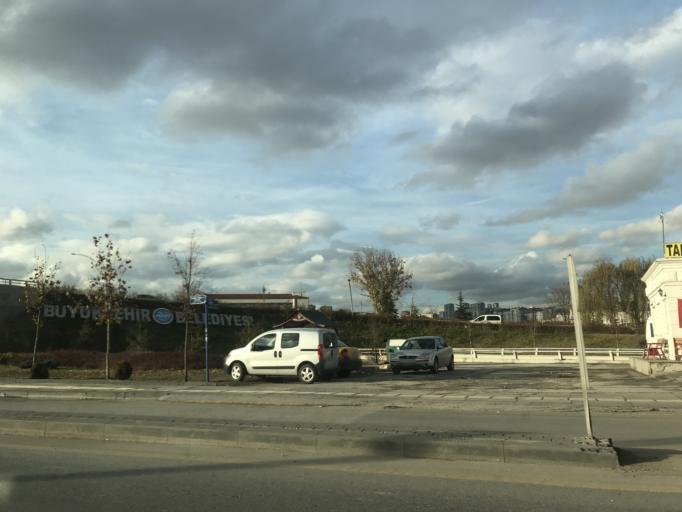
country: TR
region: Ankara
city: Ankara
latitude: 39.9591
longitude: 32.8606
